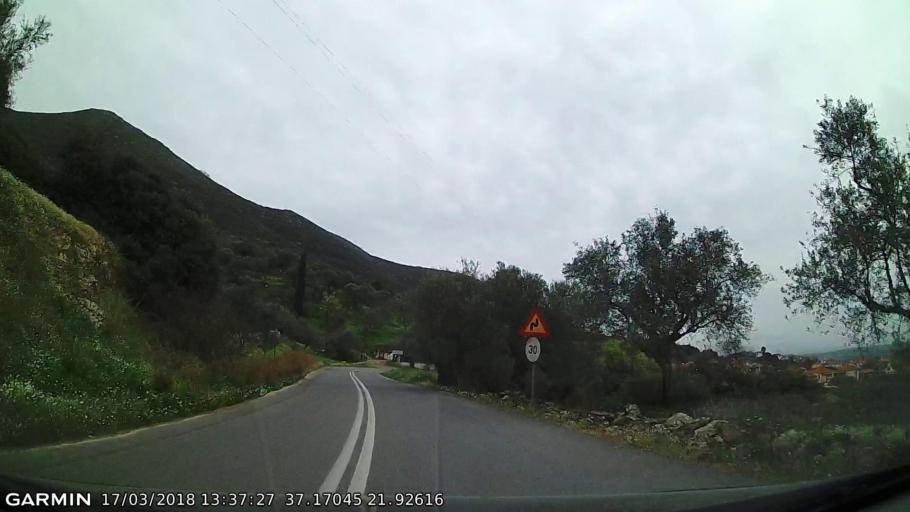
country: GR
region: Peloponnese
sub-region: Nomos Messinias
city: Meligalas
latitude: 37.1702
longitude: 21.9262
